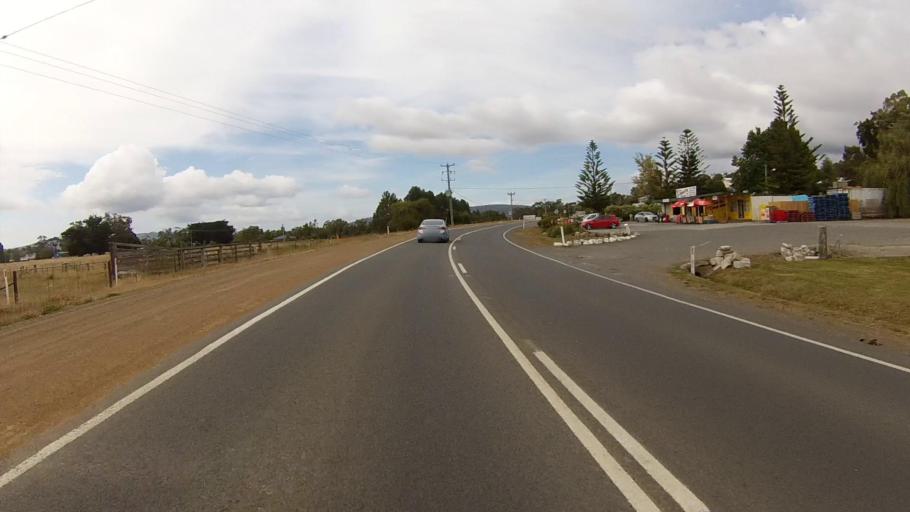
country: AU
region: Tasmania
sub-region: Kingborough
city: Margate
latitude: -43.0348
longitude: 147.2661
